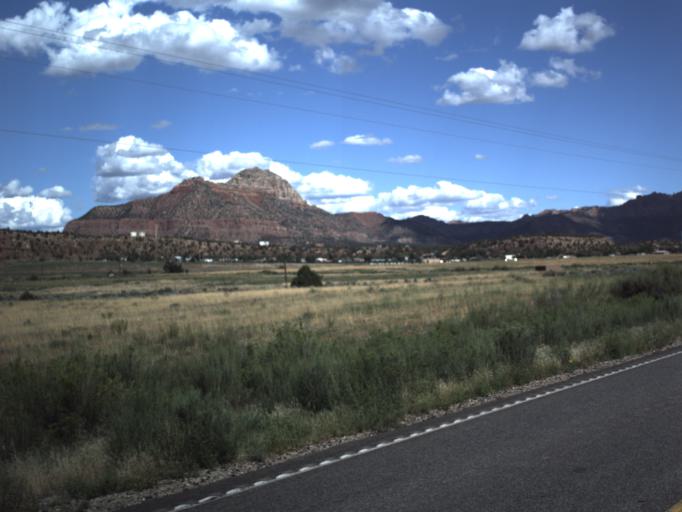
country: US
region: Utah
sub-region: Washington County
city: LaVerkin
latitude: 37.1088
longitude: -113.1436
